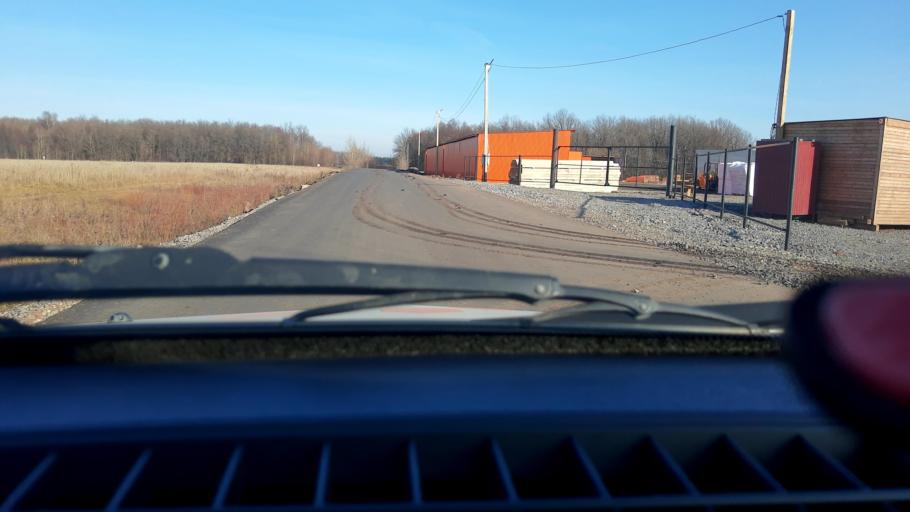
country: RU
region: Bashkortostan
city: Kabakovo
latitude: 54.6147
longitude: 56.1492
